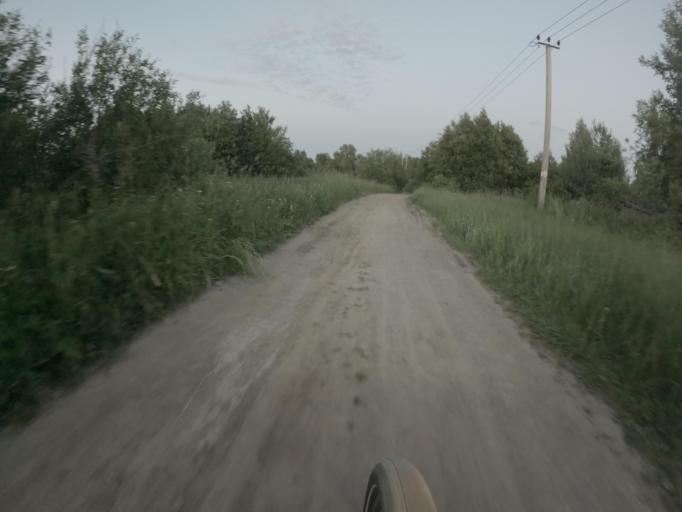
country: RU
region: Leningrad
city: Imeni Sverdlova
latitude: 59.7815
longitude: 30.6874
